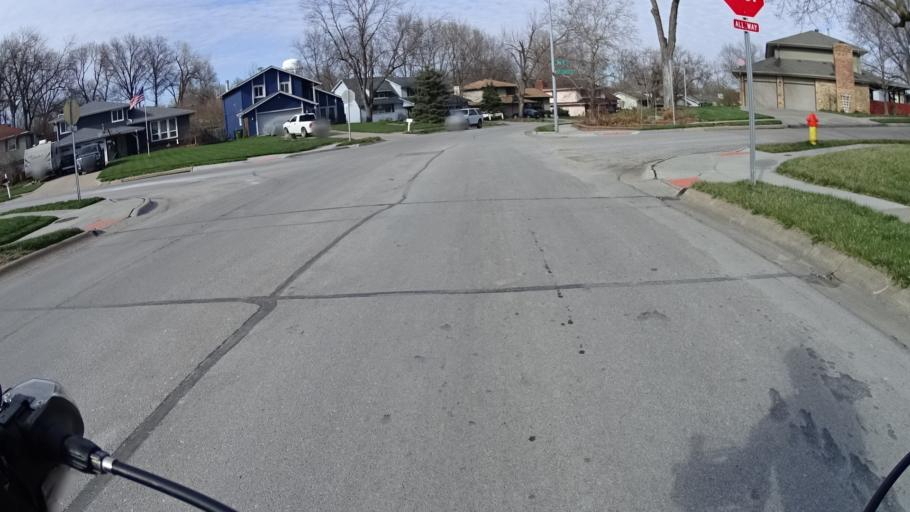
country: US
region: Nebraska
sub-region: Sarpy County
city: Offutt Air Force Base
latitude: 41.1174
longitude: -95.9583
